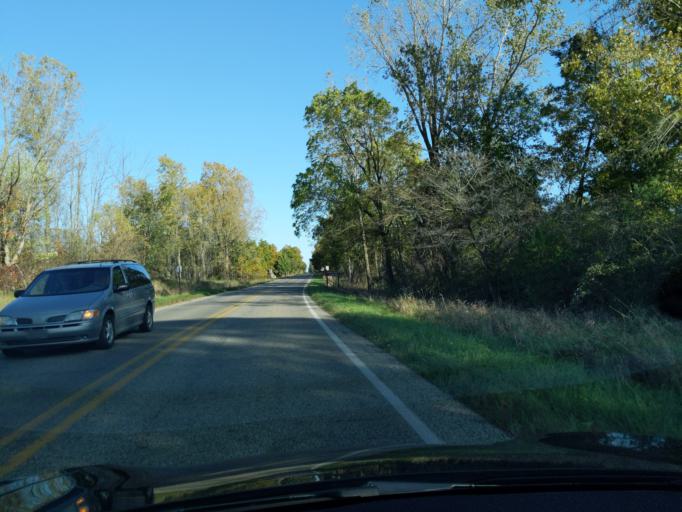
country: US
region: Michigan
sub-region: Shiawassee County
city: Laingsburg
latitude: 42.9250
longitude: -84.4125
